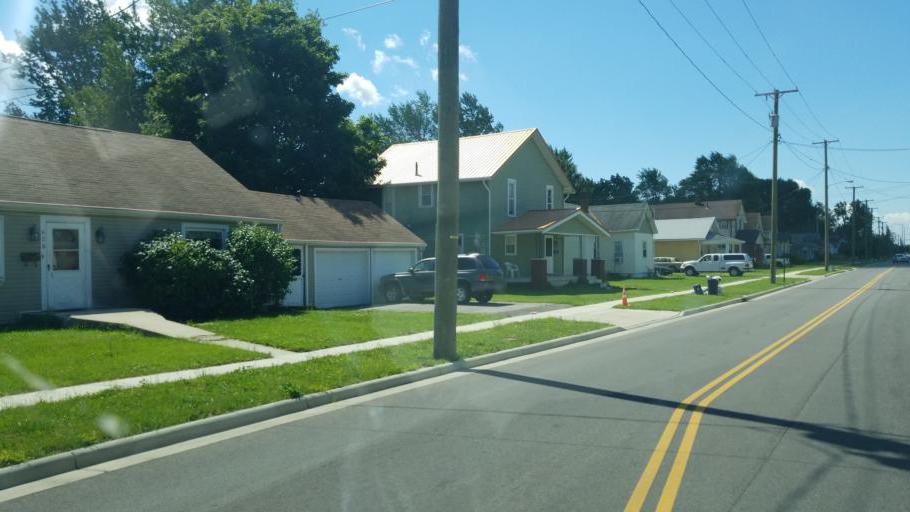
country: US
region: Ohio
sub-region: Marion County
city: Marion
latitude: 40.5999
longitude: -83.1210
